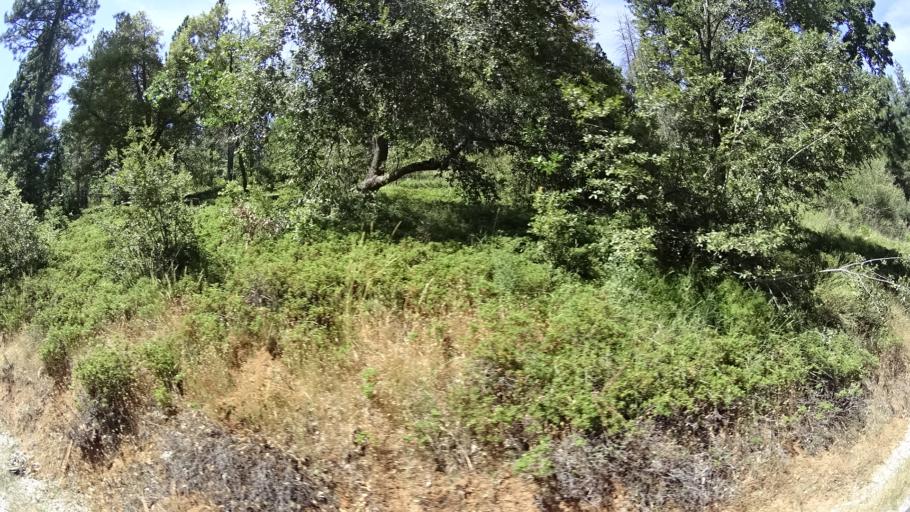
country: US
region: California
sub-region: Calaveras County
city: Forest Meadows
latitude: 38.2025
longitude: -120.3859
